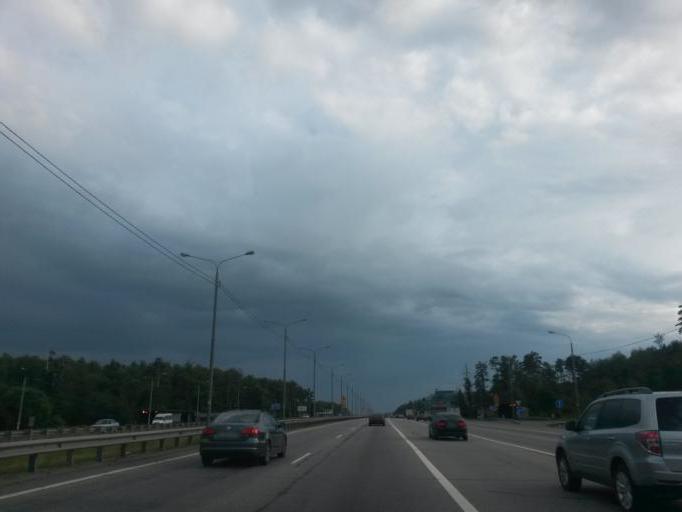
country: RU
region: Moskovskaya
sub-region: Podol'skiy Rayon
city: Podol'sk
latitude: 55.4201
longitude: 37.6103
